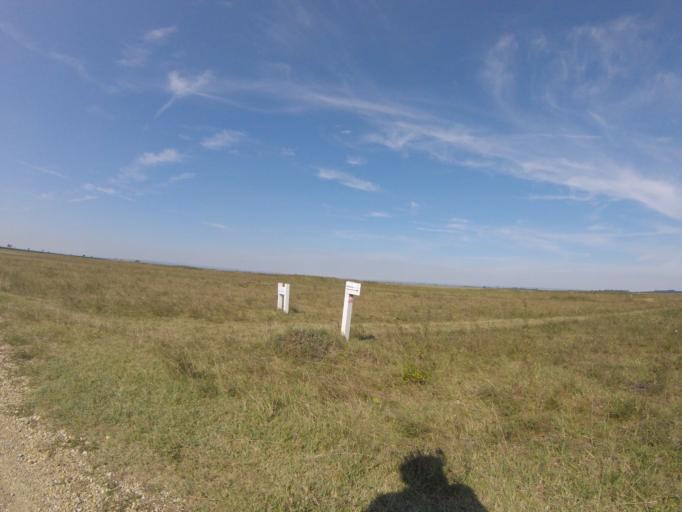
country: AT
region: Burgenland
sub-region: Politischer Bezirk Neusiedl am See
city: Apetlon
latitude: 47.7588
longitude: 16.8865
